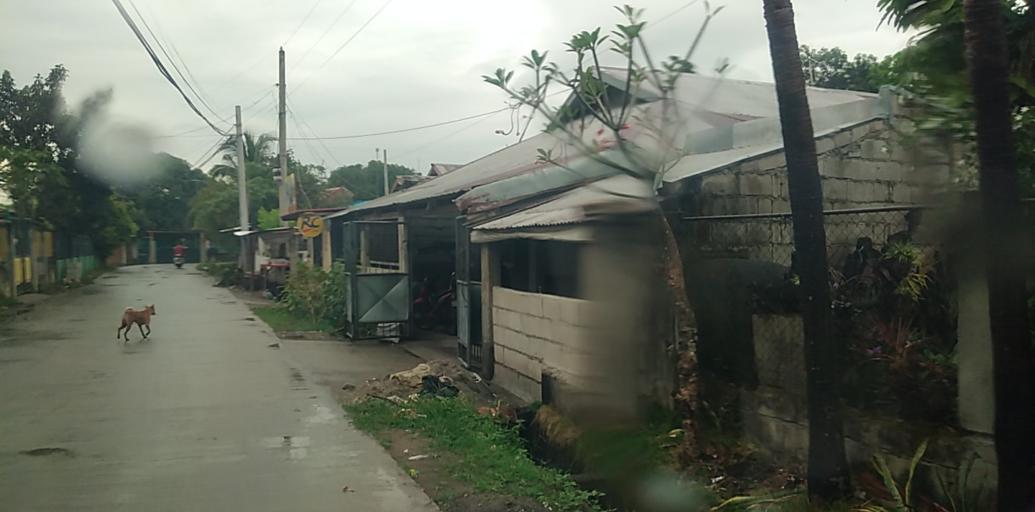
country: PH
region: Central Luzon
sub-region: Province of Pampanga
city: Anao
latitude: 15.1512
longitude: 120.7244
